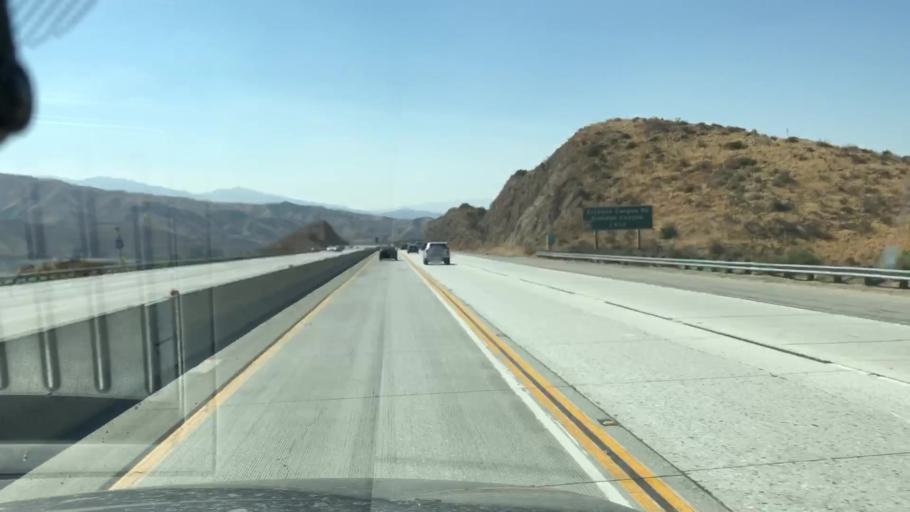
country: US
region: California
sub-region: Los Angeles County
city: Agua Dulce
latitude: 34.4406
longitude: -118.3673
